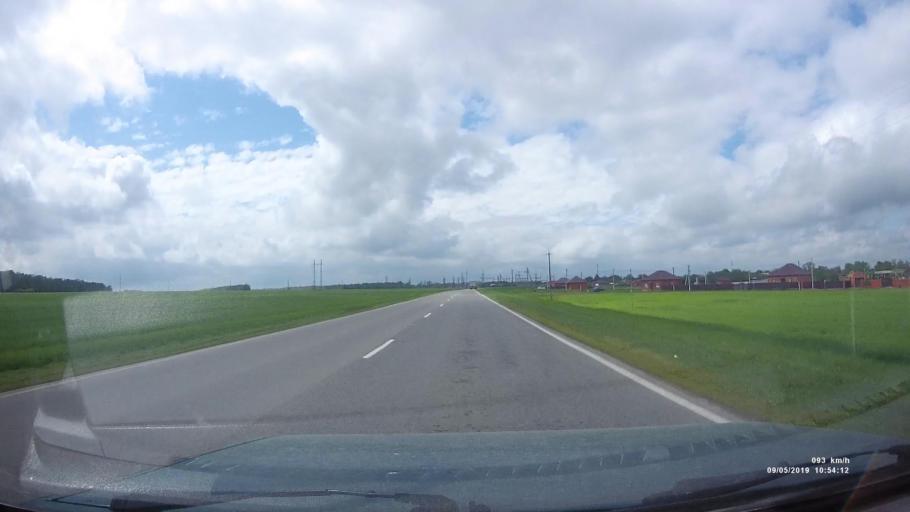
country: RU
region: Rostov
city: Peshkovo
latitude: 46.8802
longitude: 39.3334
